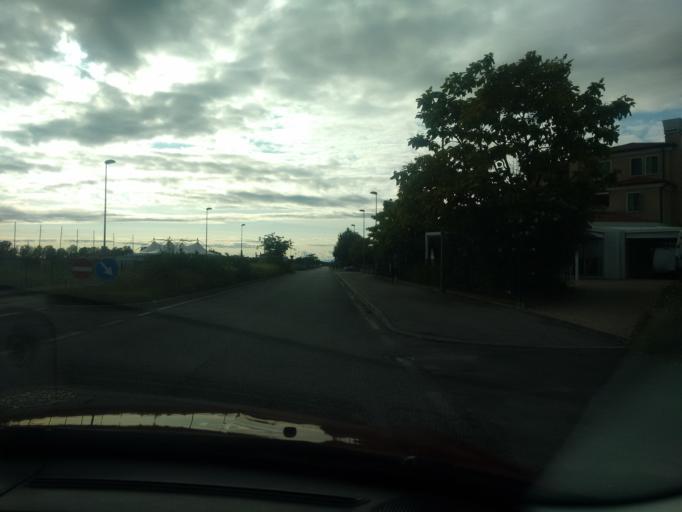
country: IT
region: Veneto
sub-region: Provincia di Venezia
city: Caorle
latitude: 45.5843
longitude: 12.8430
